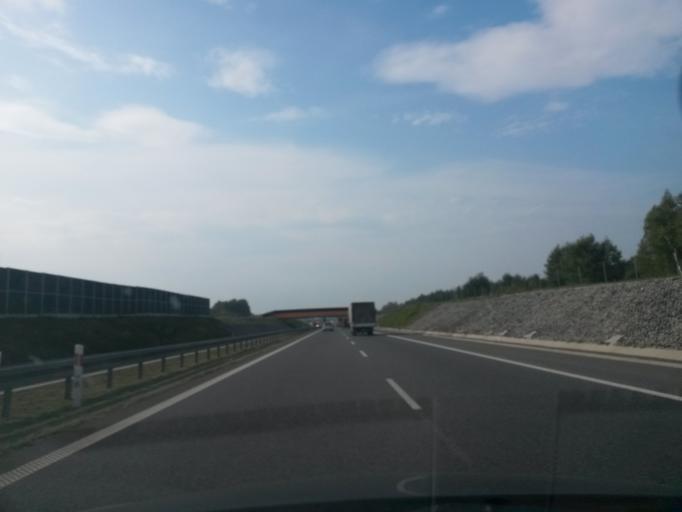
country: PL
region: Lesser Poland Voivodeship
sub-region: Powiat bochenski
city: Jodlowka
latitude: 49.9990
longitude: 20.5555
